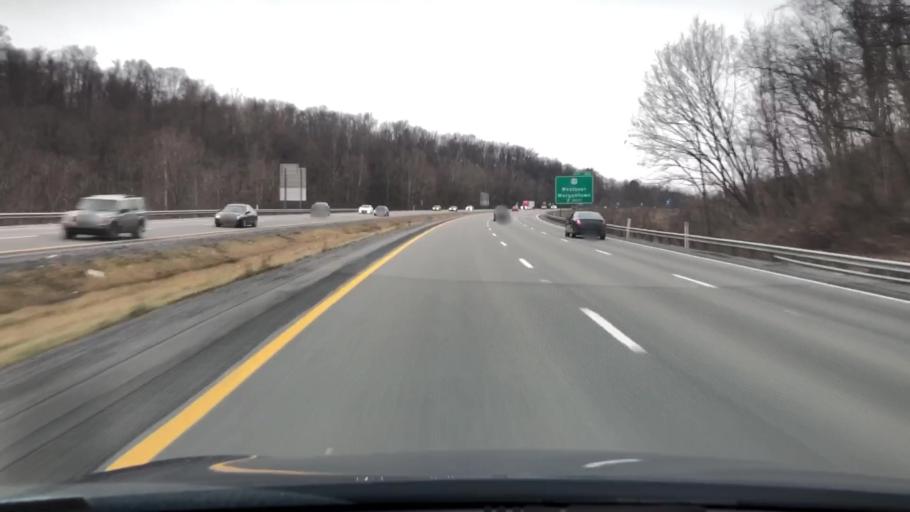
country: US
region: West Virginia
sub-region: Monongalia County
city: Westover
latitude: 39.5973
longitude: -79.9868
